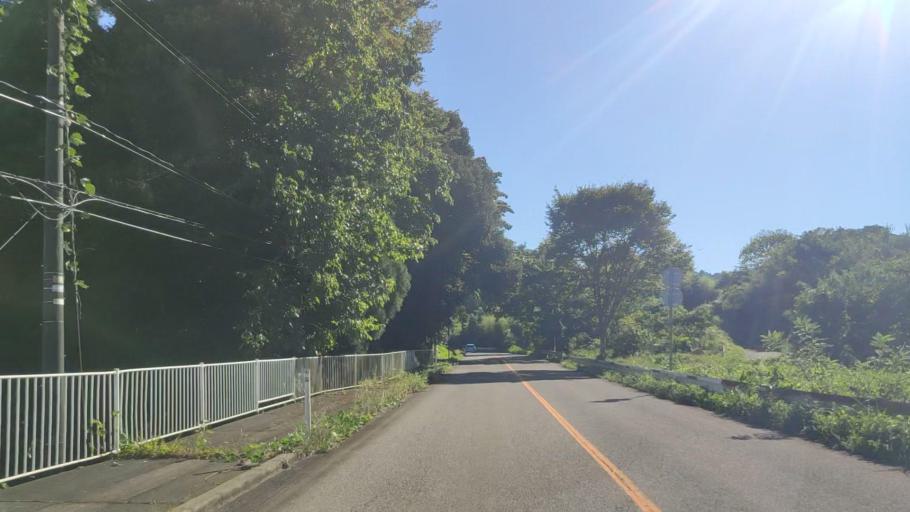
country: JP
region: Ishikawa
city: Nanao
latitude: 37.2628
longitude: 137.0895
